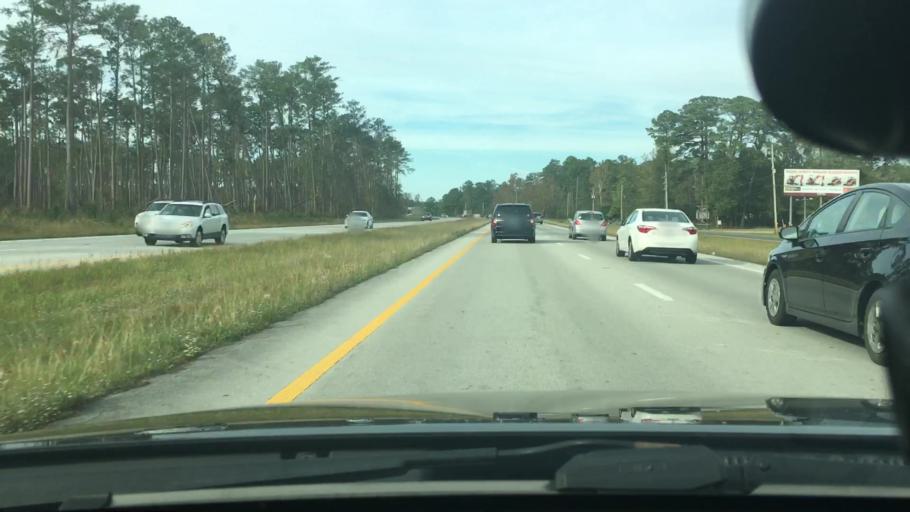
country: US
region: North Carolina
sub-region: Craven County
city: Neuse Forest
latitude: 34.9431
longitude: -76.9487
